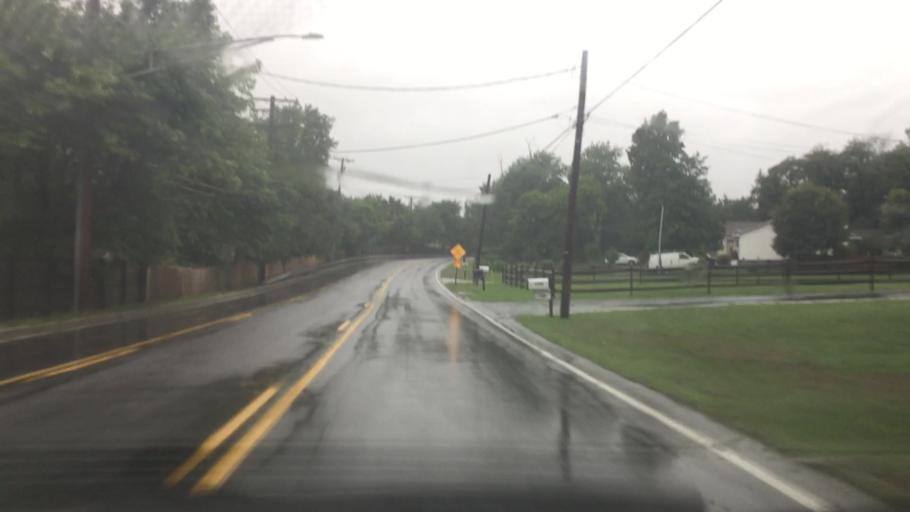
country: US
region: Maryland
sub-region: Anne Arundel County
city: Severn
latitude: 39.1380
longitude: -76.7211
